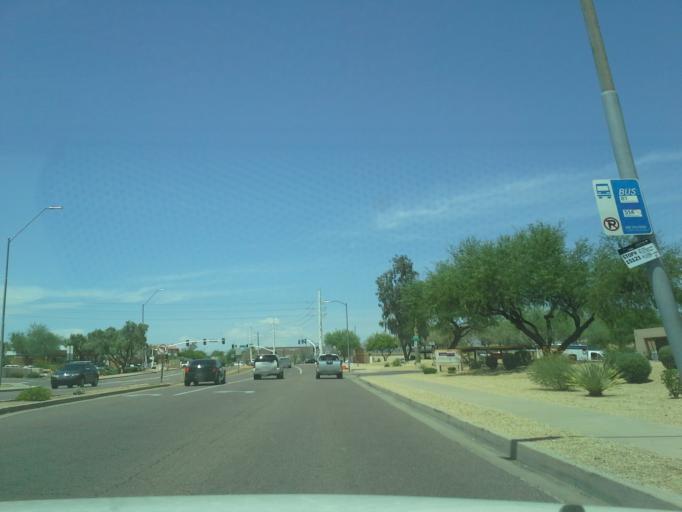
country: US
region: Arizona
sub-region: Maricopa County
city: Scottsdale
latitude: 33.5809
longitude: -111.8863
